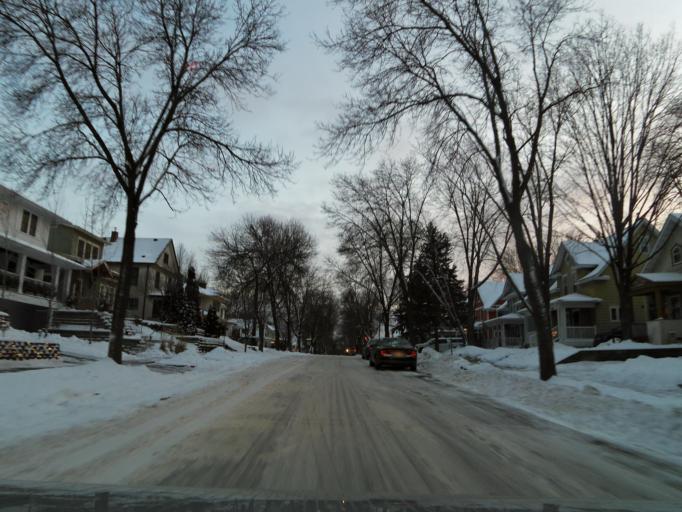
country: US
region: Minnesota
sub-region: Hennepin County
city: Saint Louis Park
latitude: 44.9224
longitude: -93.3215
